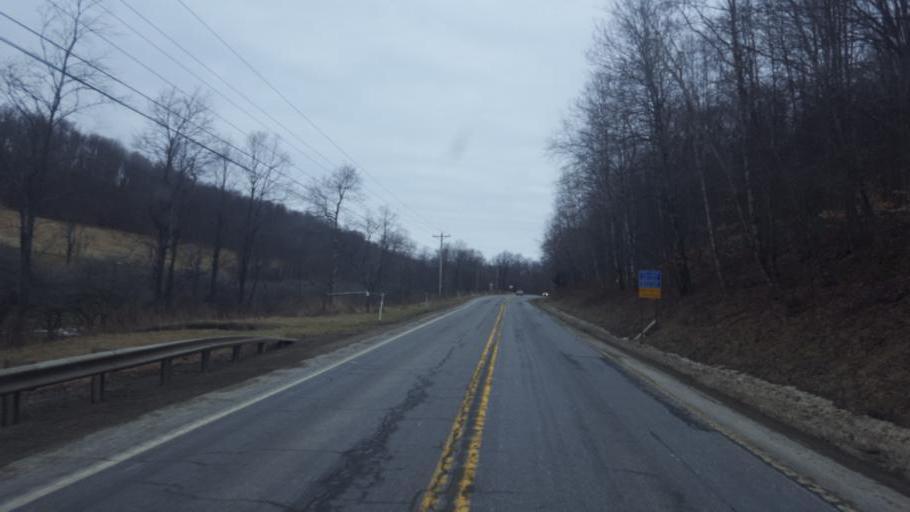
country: US
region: Pennsylvania
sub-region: Potter County
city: Coudersport
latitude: 41.8333
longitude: -77.9059
